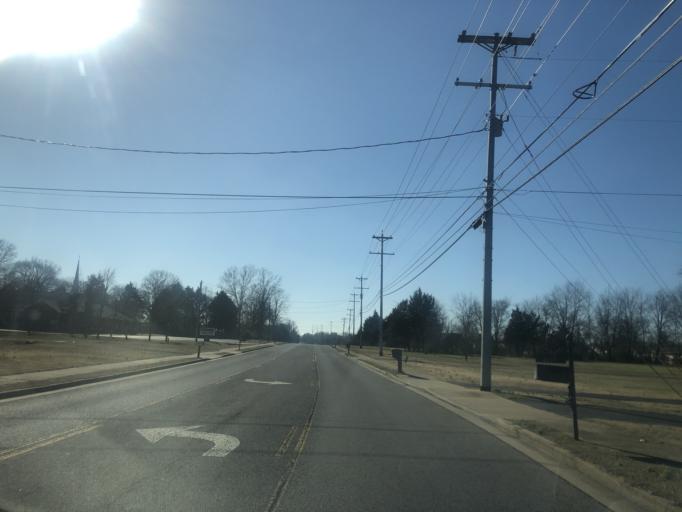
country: US
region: Tennessee
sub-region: Rutherford County
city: Smyrna
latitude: 35.9126
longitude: -86.4711
